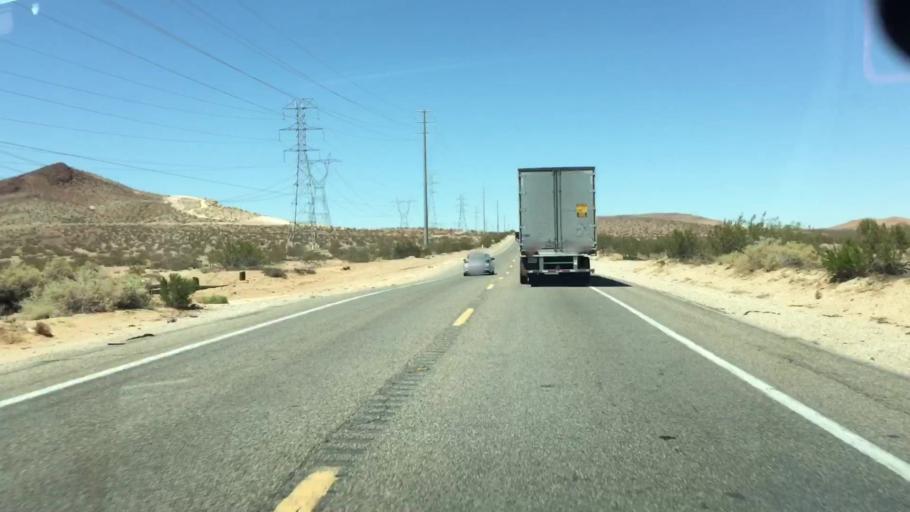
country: US
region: California
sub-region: Kern County
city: Boron
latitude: 34.8604
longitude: -117.5050
